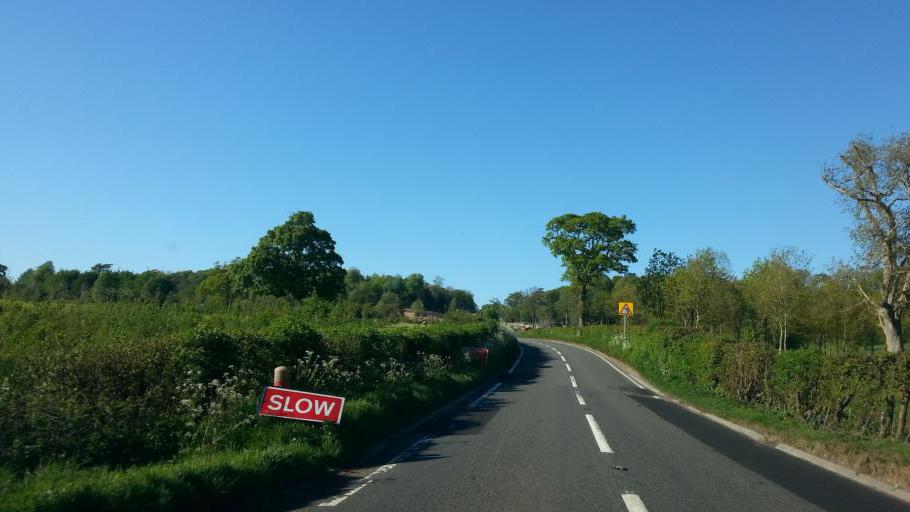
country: GB
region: England
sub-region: Somerset
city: Castle Cary
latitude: 51.0722
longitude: -2.4855
